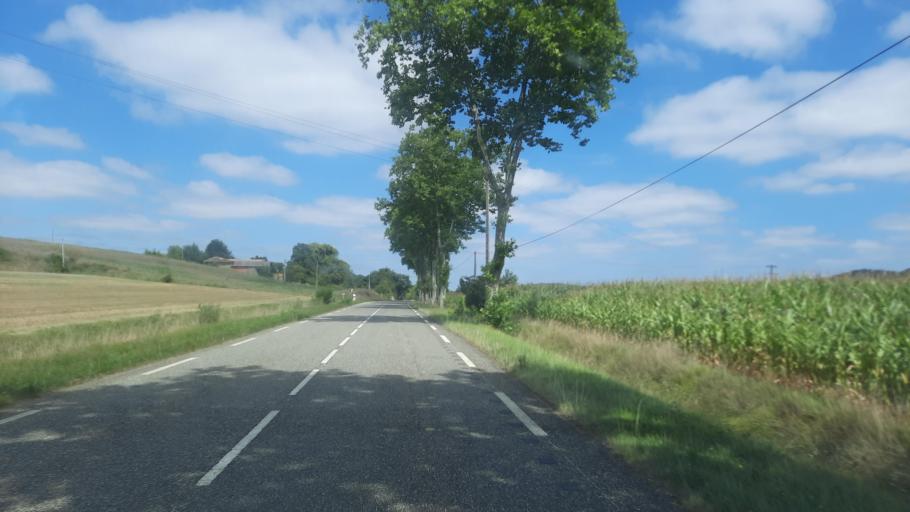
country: FR
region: Midi-Pyrenees
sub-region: Departement de la Haute-Garonne
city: Boulogne-sur-Gesse
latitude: 43.3609
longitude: 0.7342
